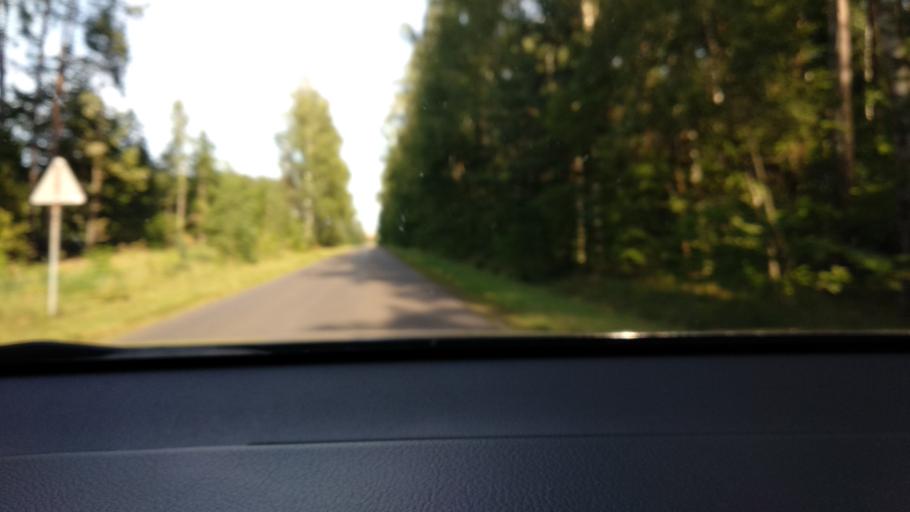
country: PL
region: Masovian Voivodeship
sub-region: Powiat pultuski
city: Obryte
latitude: 52.7137
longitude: 21.1724
